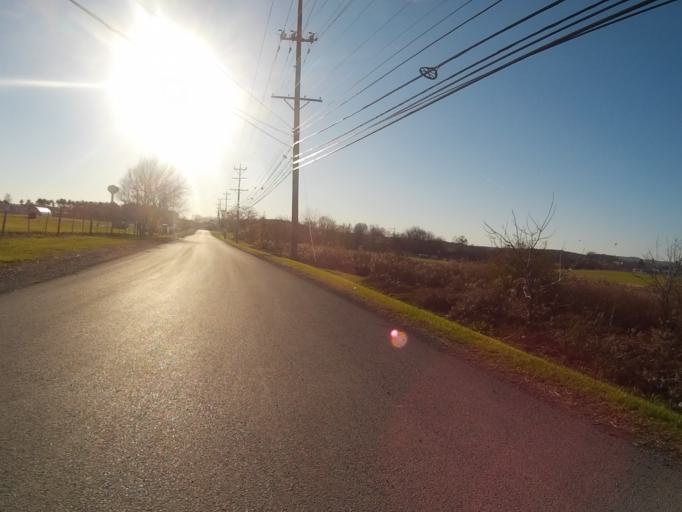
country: US
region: Pennsylvania
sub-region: Centre County
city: Houserville
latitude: 40.8215
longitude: -77.8546
